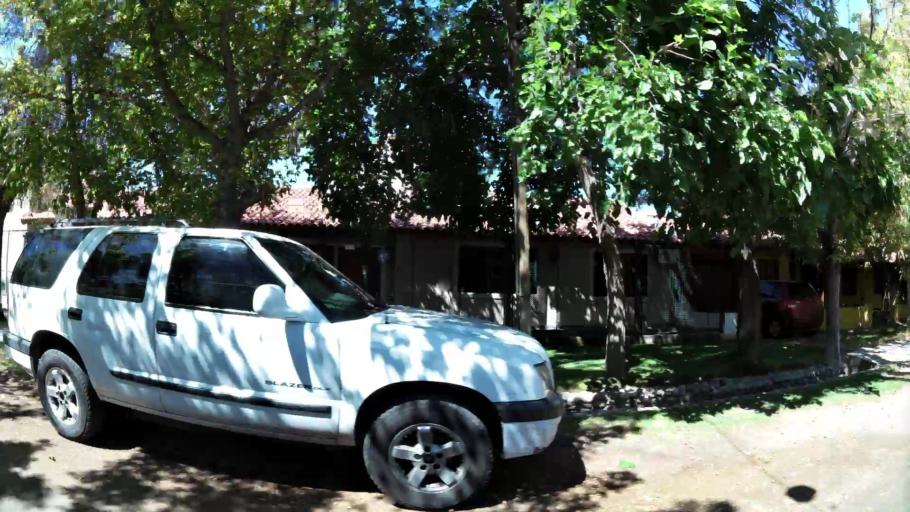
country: AR
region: Mendoza
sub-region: Departamento de Godoy Cruz
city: Godoy Cruz
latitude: -32.9686
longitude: -68.8707
